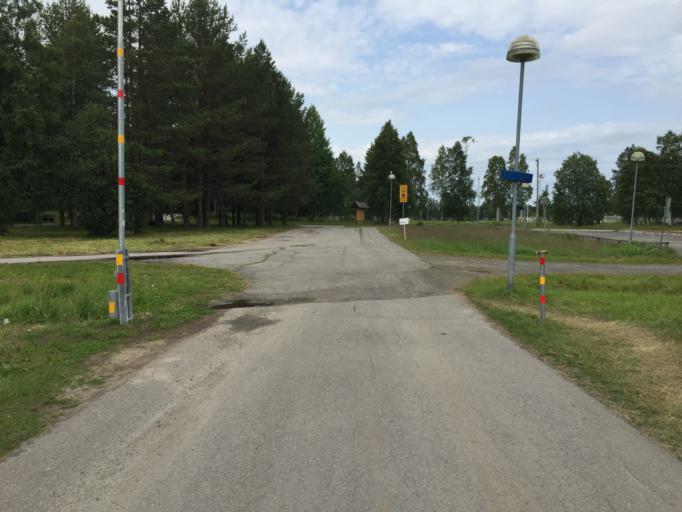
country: SE
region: Vaesterbotten
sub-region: Umea Kommun
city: Ersmark
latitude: 63.8380
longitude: 20.3396
